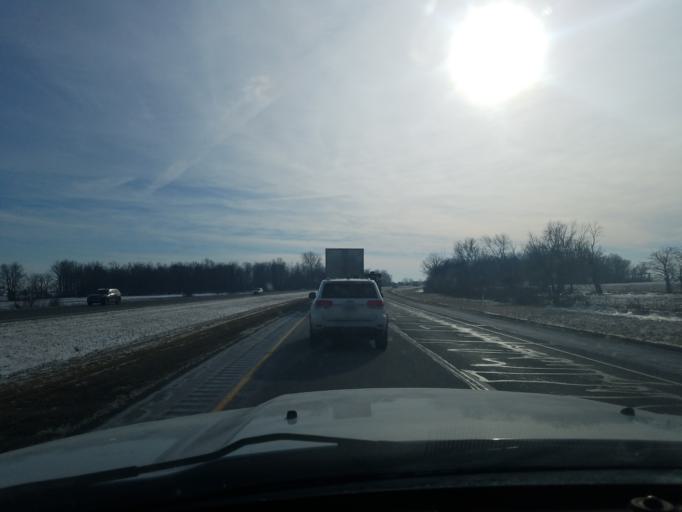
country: US
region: Indiana
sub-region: Huntington County
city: Markle
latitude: 40.7796
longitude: -85.3845
